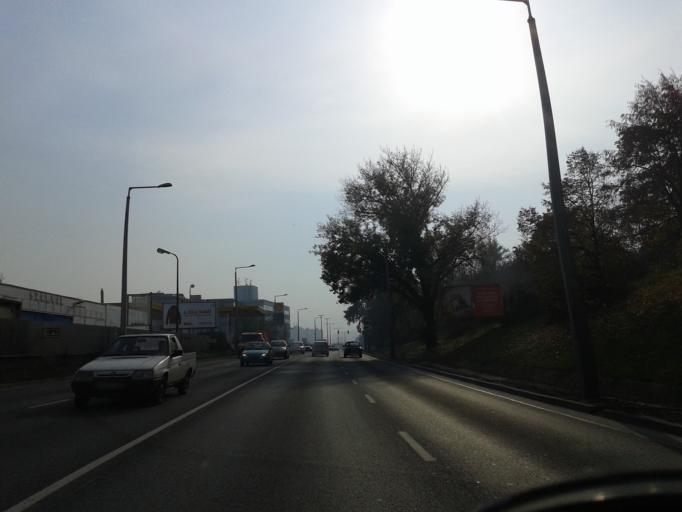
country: HU
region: Budapest
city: Budapest III. keruelet
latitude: 47.5541
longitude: 19.0275
